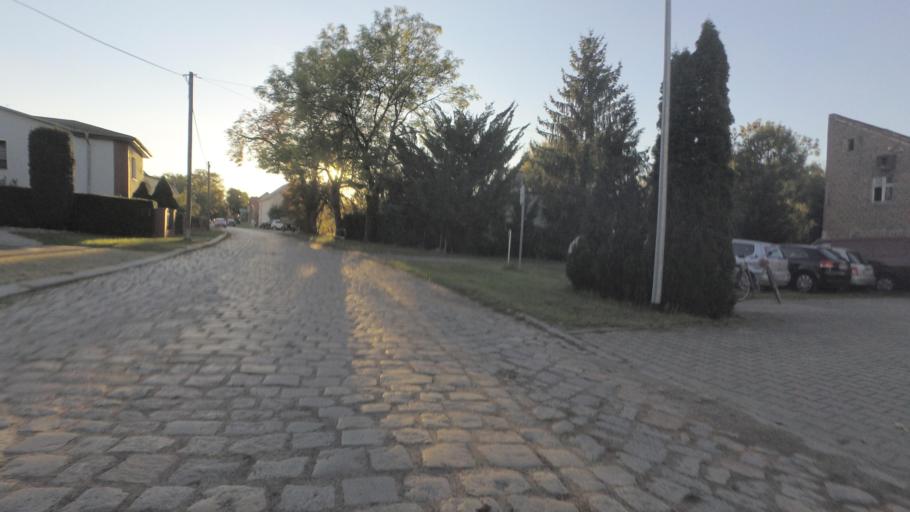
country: DE
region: Brandenburg
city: Ludwigsfelde
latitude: 52.2721
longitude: 13.3100
